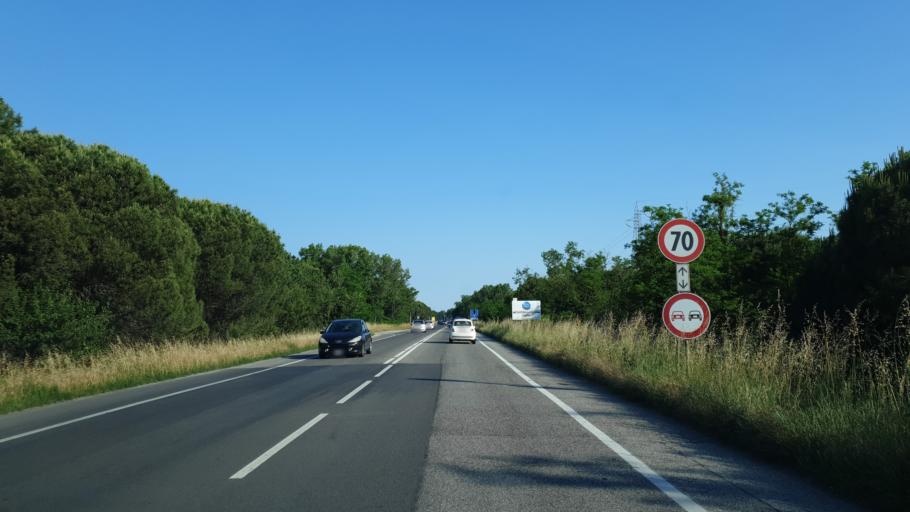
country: IT
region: Emilia-Romagna
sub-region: Provincia di Ravenna
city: Fosso Ghiaia
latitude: 44.3421
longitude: 12.2655
